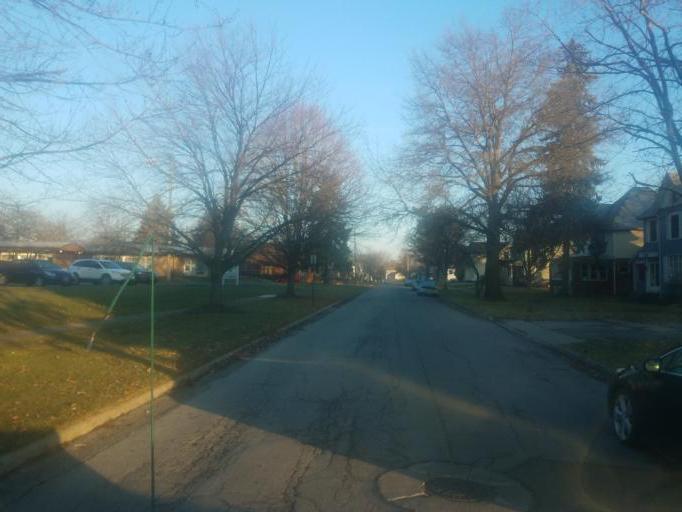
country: US
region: Ohio
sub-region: Crawford County
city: Bucyrus
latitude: 40.8007
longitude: -82.9728
